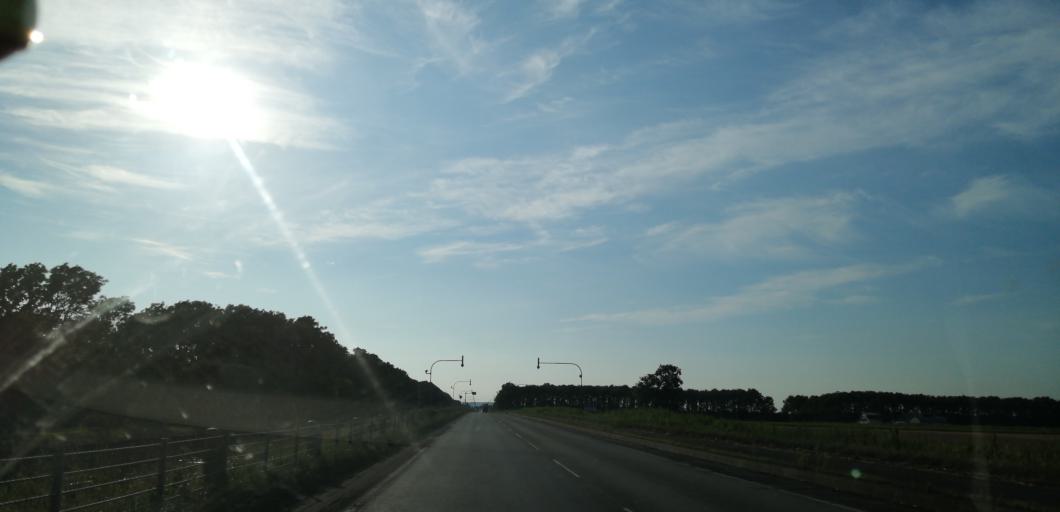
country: JP
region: Hokkaido
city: Kitahiroshima
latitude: 42.9763
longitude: 141.6459
